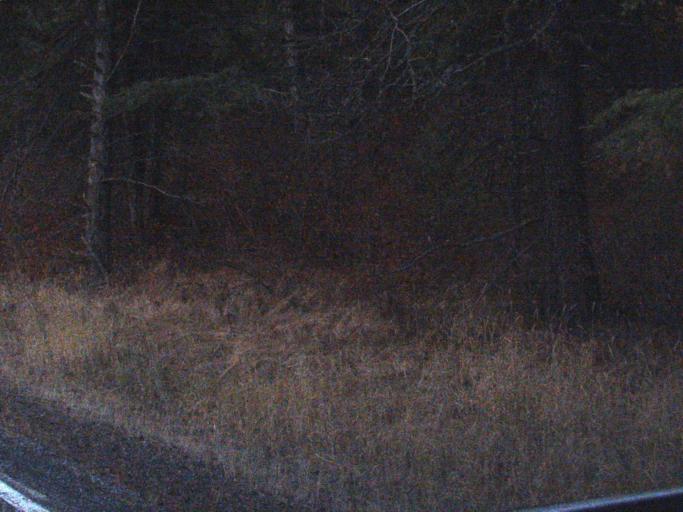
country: US
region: Washington
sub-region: Ferry County
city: Republic
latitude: 48.3571
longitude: -118.7418
